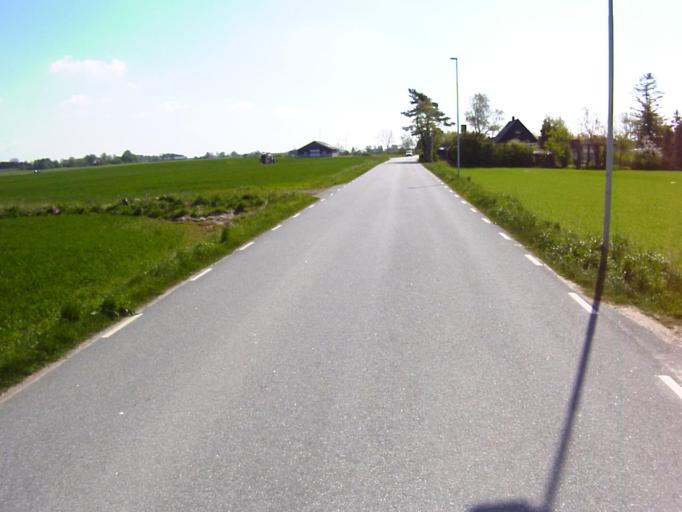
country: SE
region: Skane
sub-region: Kristianstads Kommun
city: Kristianstad
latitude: 56.0207
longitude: 14.2175
